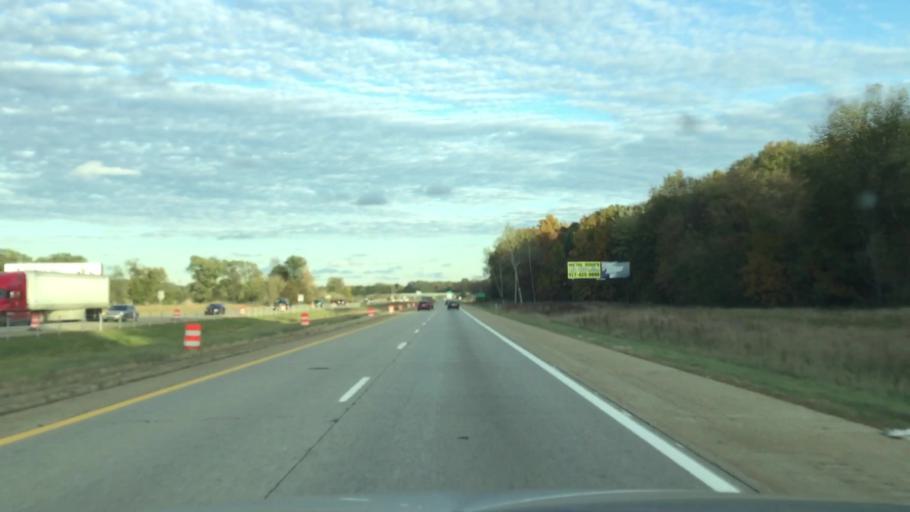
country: US
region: Michigan
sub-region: Calhoun County
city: Albion
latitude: 42.2640
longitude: -84.7214
